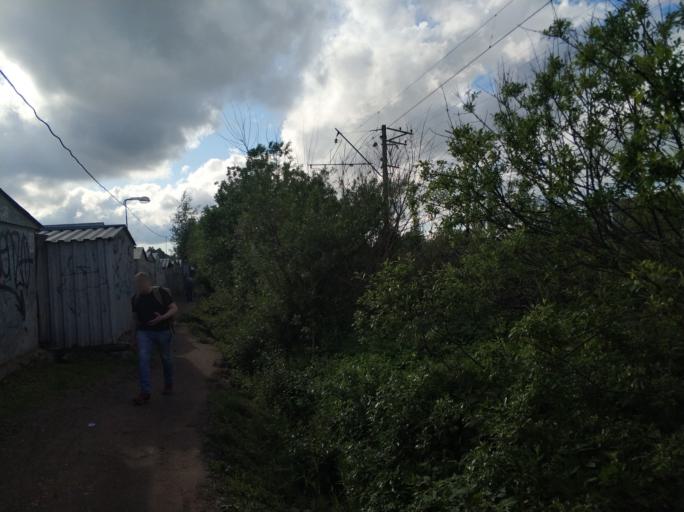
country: RU
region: Leningrad
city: Murino
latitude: 60.0432
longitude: 30.4299
